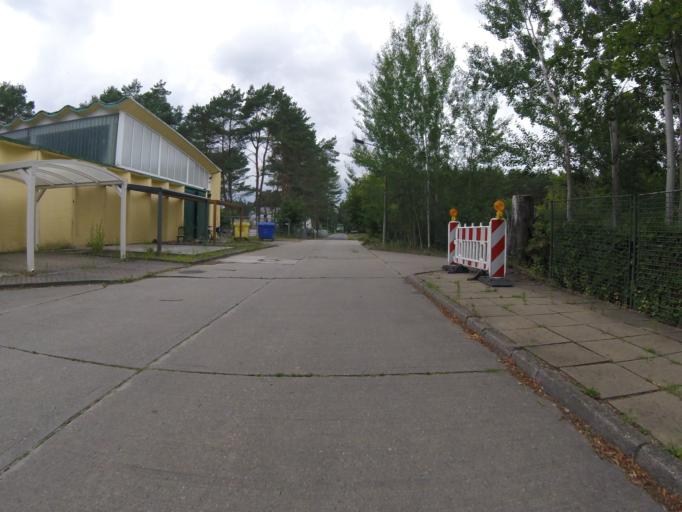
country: DE
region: Brandenburg
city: Bestensee
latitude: 52.2439
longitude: 13.6432
